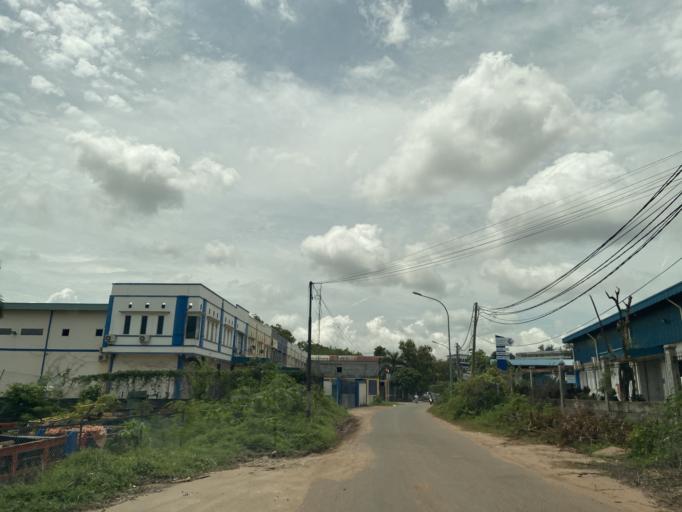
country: SG
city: Singapore
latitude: 1.1614
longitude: 104.0064
